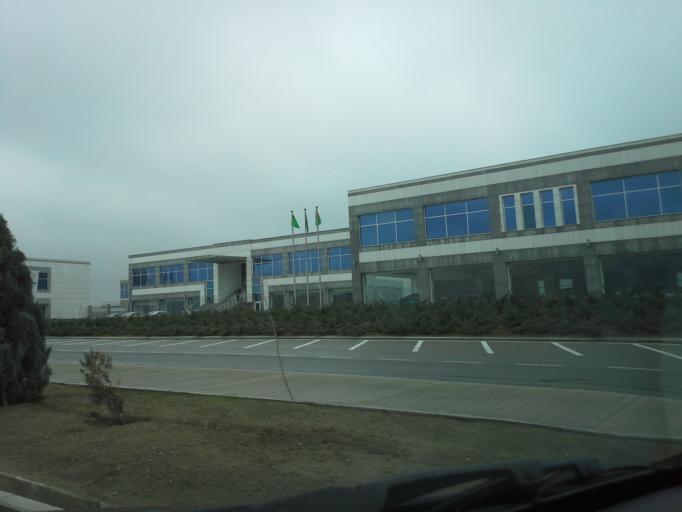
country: TM
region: Ahal
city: Ashgabat
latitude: 37.9509
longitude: 58.4344
